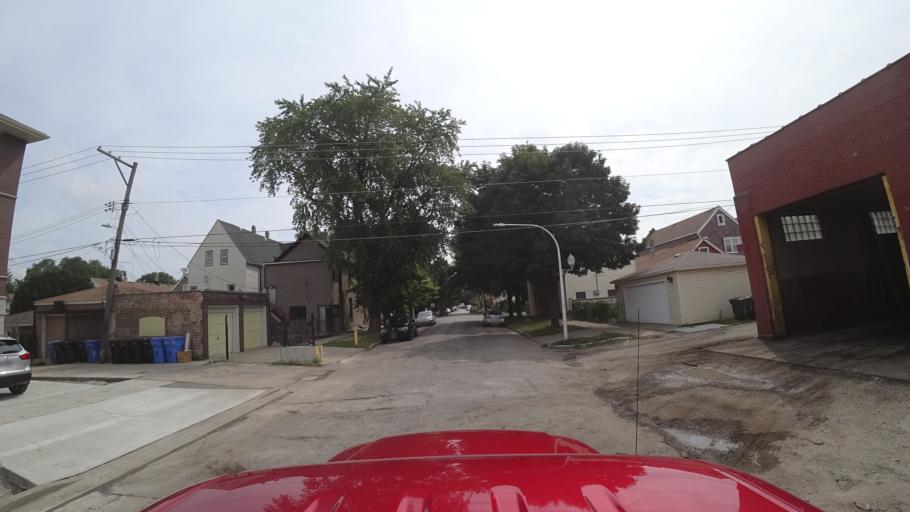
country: US
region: Illinois
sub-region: Cook County
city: Chicago
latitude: 41.8332
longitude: -87.6714
